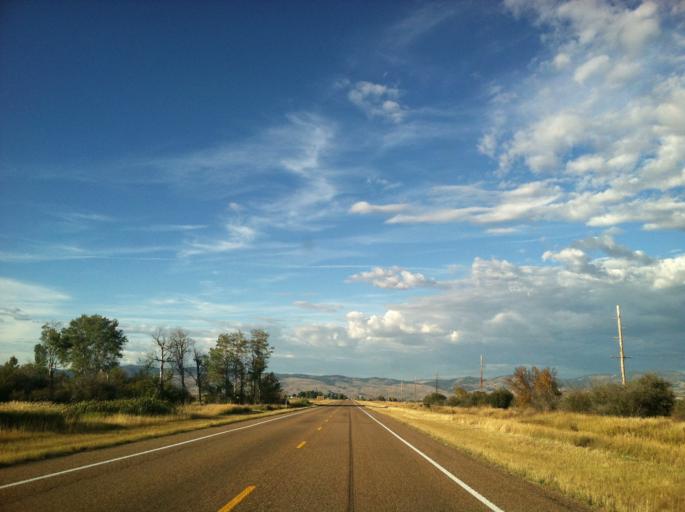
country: US
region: Montana
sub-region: Granite County
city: Philipsburg
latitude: 46.5674
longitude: -113.2087
